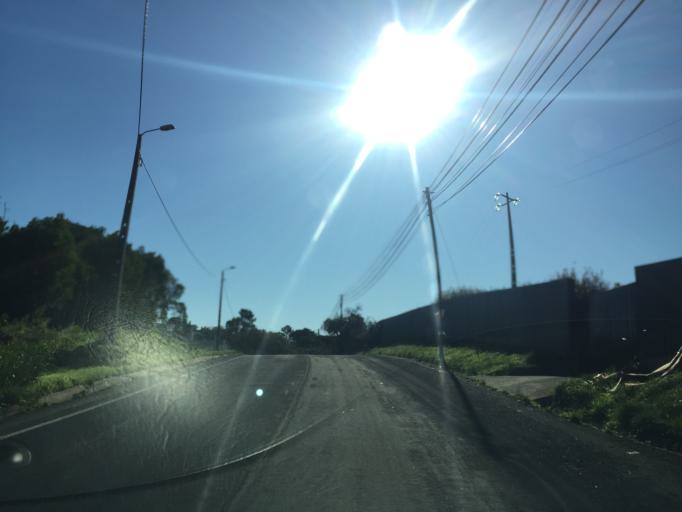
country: PT
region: Lisbon
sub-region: Sintra
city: Belas
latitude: 38.7954
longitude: -9.2683
